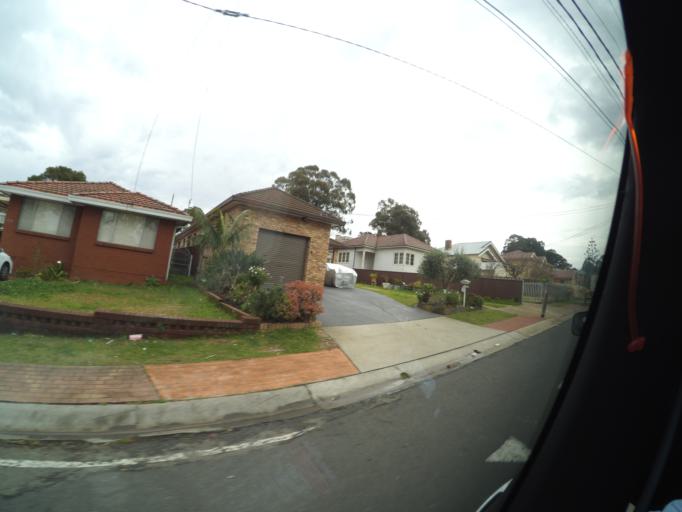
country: AU
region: New South Wales
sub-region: Bankstown
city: Bankstown
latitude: -33.9163
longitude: 151.0187
